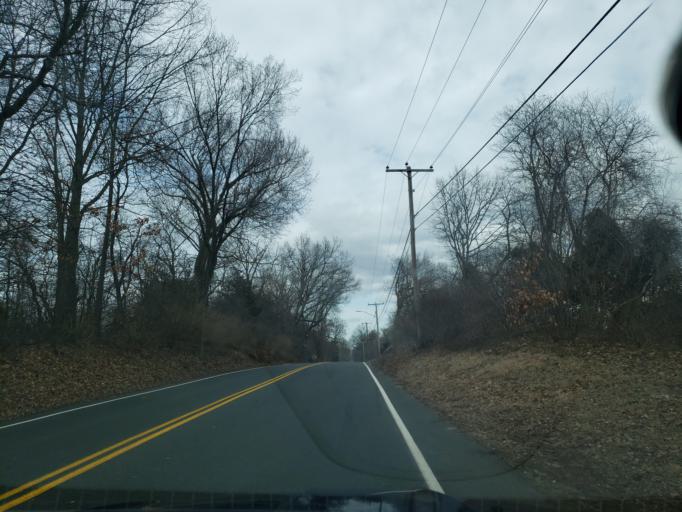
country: US
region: Connecticut
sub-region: Middlesex County
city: Cromwell
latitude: 41.6527
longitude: -72.6631
